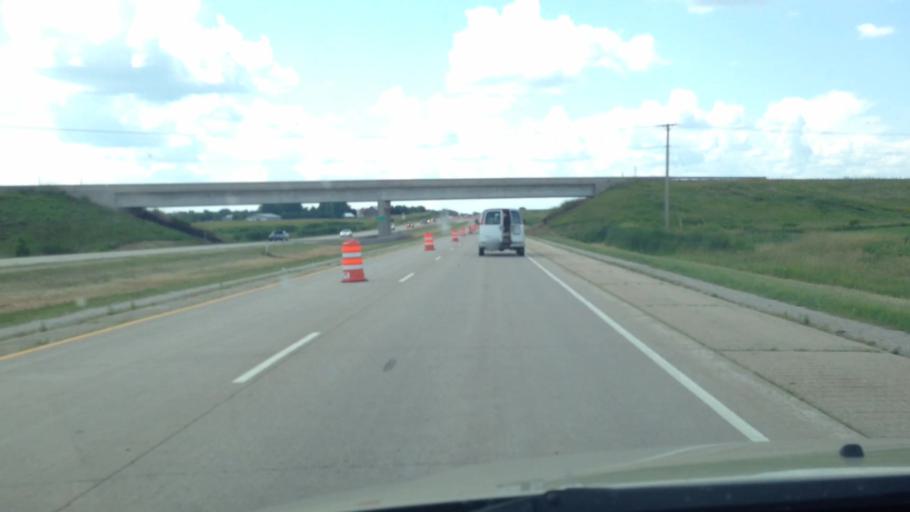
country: US
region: Wisconsin
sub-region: Brown County
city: Pulaski
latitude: 44.6888
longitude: -88.3222
